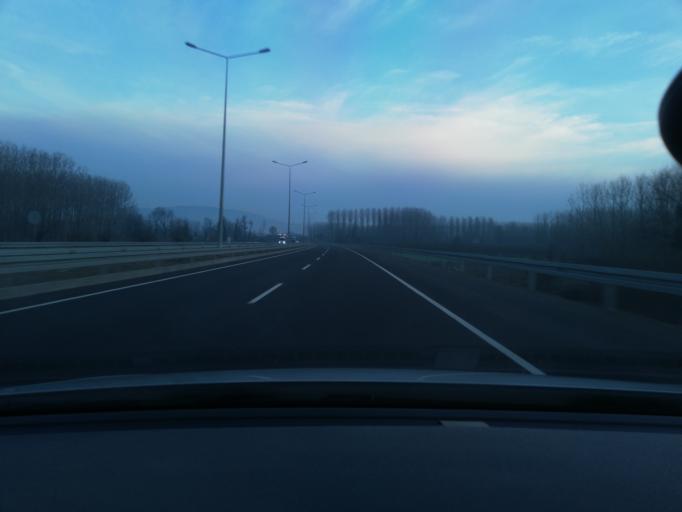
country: TR
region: Duzce
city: Duzce
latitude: 40.8109
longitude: 31.1691
